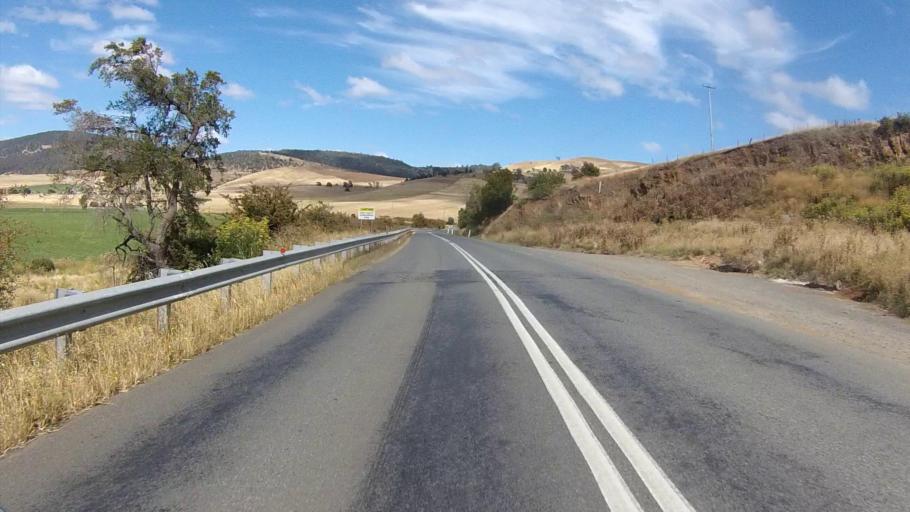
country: AU
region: Tasmania
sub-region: Brighton
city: Bridgewater
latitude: -42.5843
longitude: 147.4121
